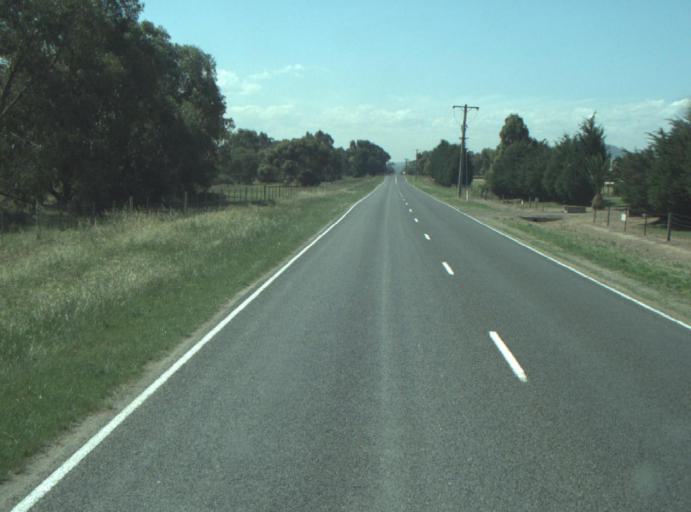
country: AU
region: Victoria
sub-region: Greater Geelong
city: Lara
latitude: -38.0152
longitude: 144.3977
